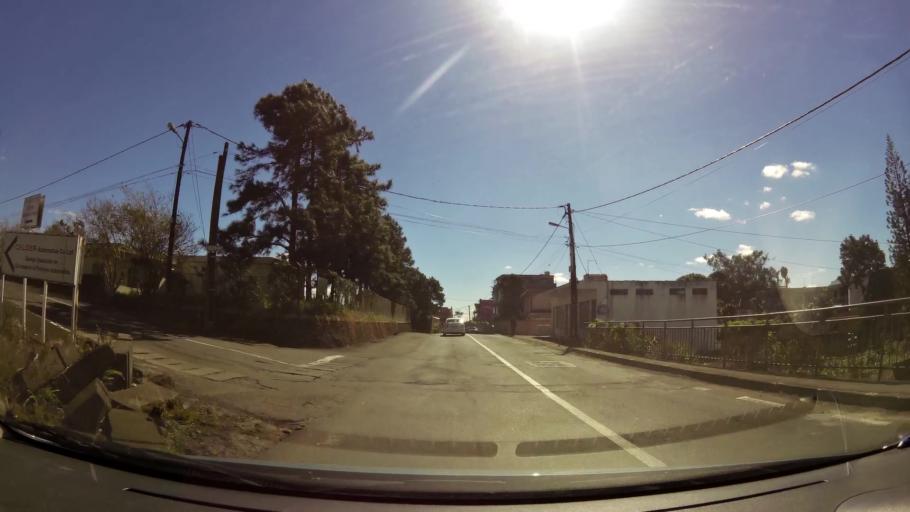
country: MU
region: Plaines Wilhems
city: Vacoas
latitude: -20.3282
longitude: 57.4861
